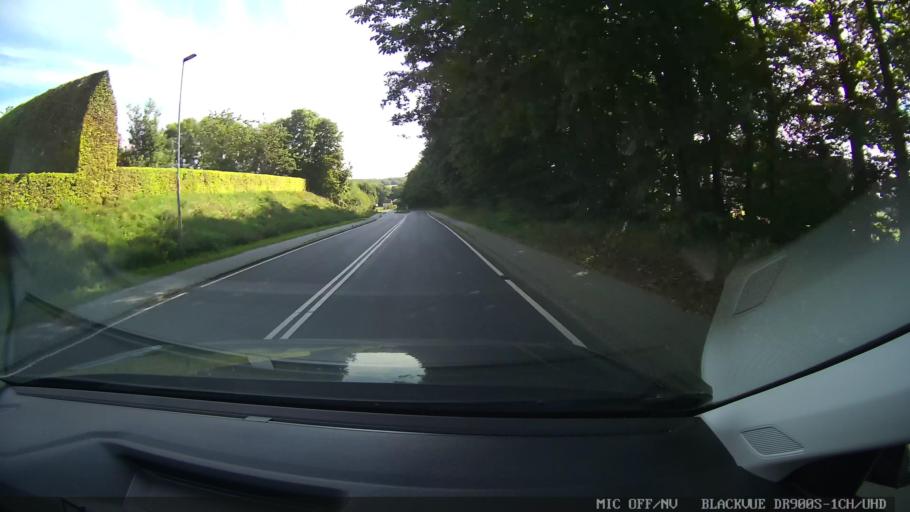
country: DK
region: North Denmark
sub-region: Mariagerfjord Kommune
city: Arden
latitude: 56.7822
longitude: 9.7136
